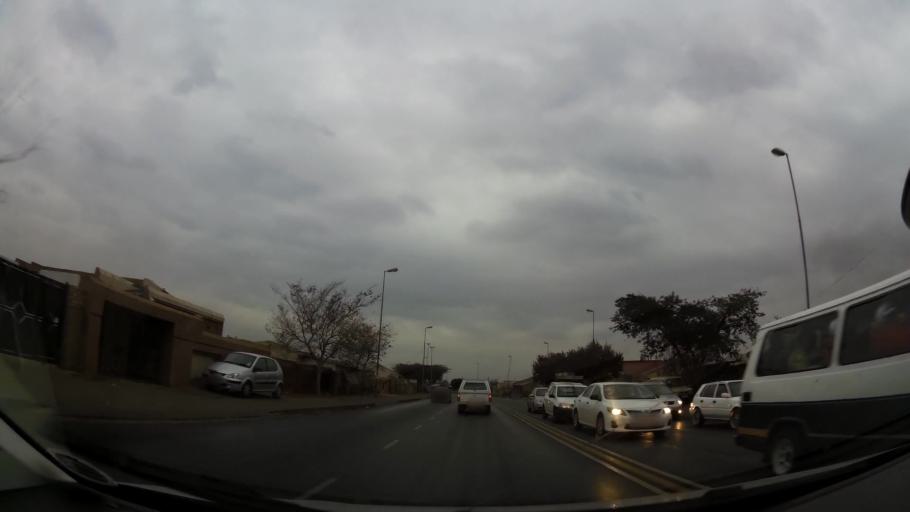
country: ZA
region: Gauteng
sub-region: City of Johannesburg Metropolitan Municipality
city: Soweto
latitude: -26.2654
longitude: 27.8581
